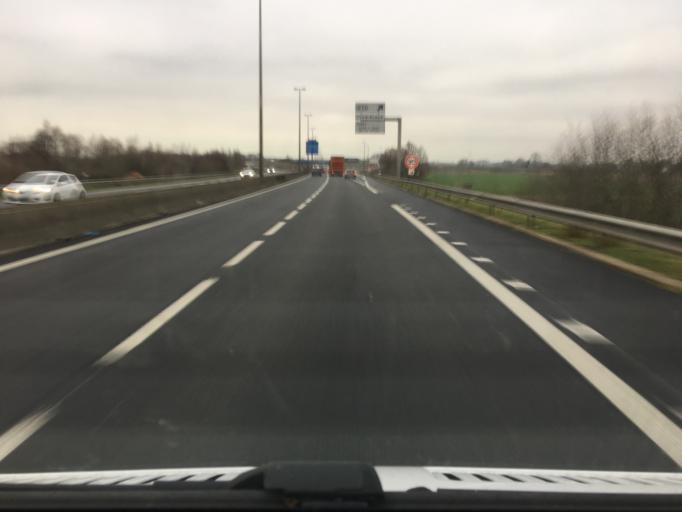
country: FR
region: Nord-Pas-de-Calais
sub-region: Departement du Nord
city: Loon-Plage
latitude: 50.9675
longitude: 2.2198
